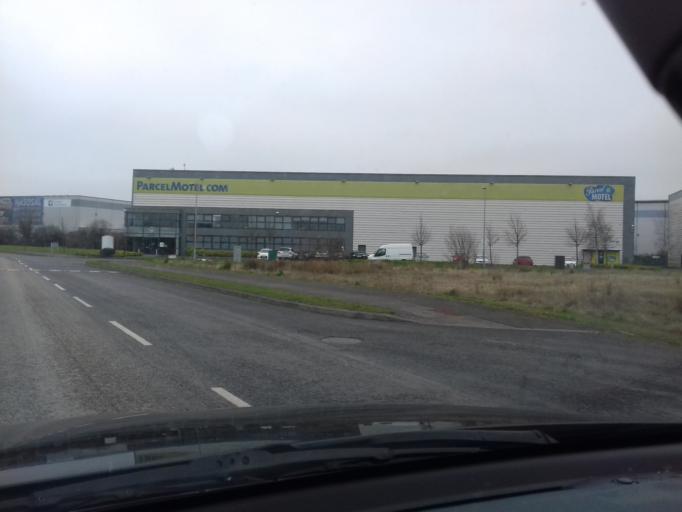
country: IE
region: Leinster
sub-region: Dublin City
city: Finglas
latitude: 53.3991
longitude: -6.3209
